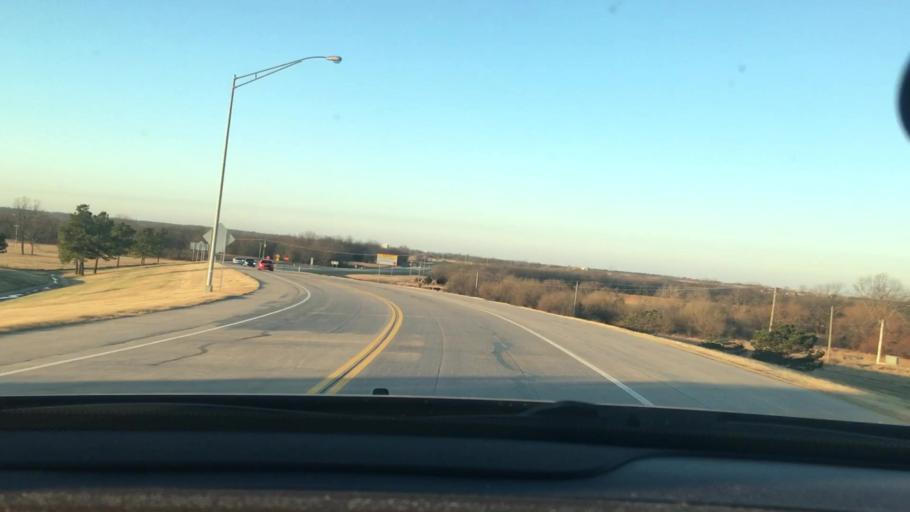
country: US
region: Oklahoma
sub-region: Pontotoc County
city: Ada
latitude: 34.6568
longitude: -96.7976
